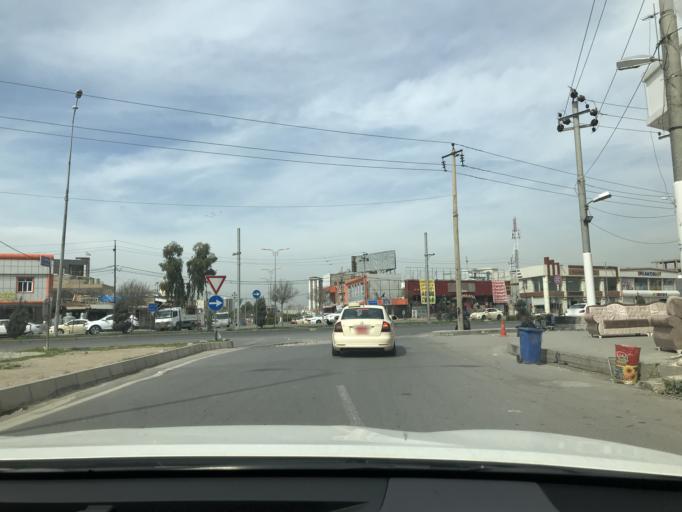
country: IQ
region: Arbil
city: Erbil
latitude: 36.1730
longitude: 44.0382
